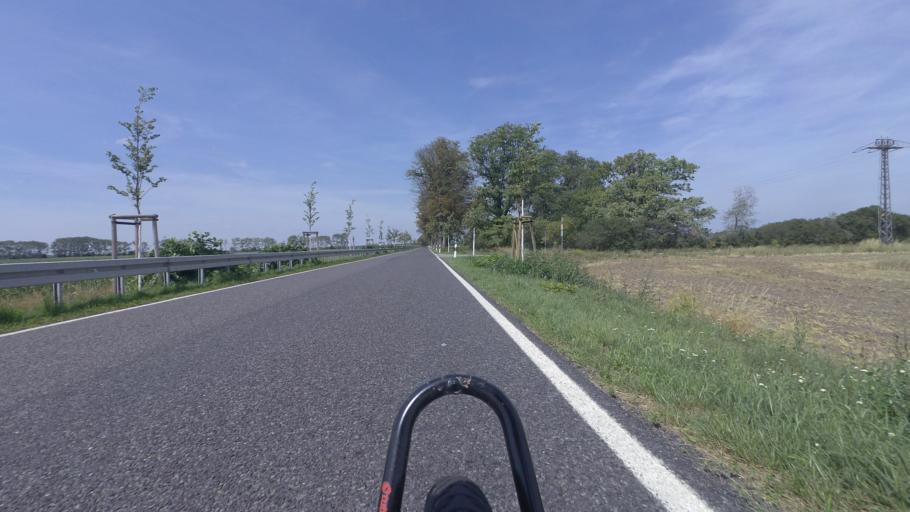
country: DE
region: Brandenburg
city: Rhinow
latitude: 52.7636
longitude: 12.2881
